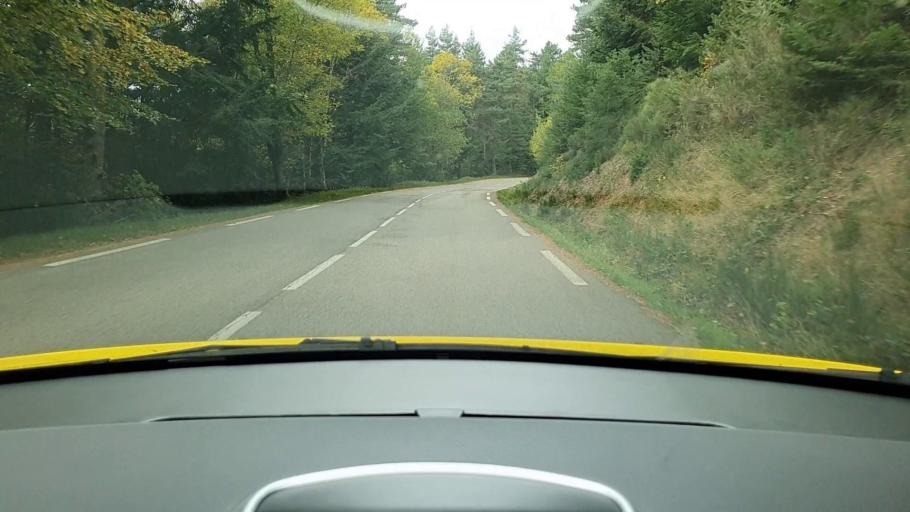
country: FR
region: Languedoc-Roussillon
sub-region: Departement de la Lozere
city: Meyrueis
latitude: 44.1272
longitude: 3.4369
